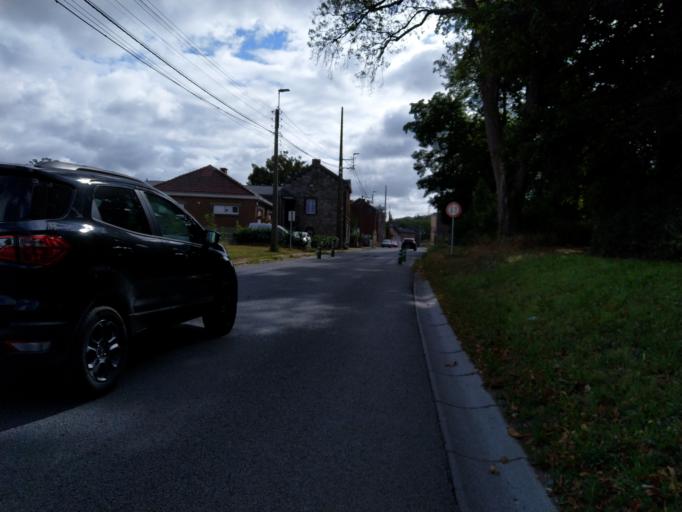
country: BE
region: Wallonia
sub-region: Province de Liege
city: Flemalle-Haute
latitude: 50.5839
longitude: 5.4414
